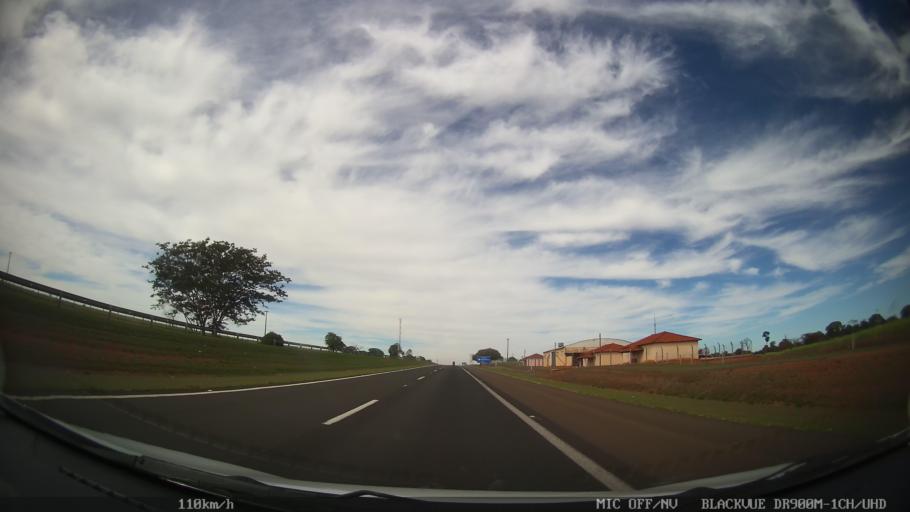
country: BR
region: Sao Paulo
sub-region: Taquaritinga
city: Taquaritinga
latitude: -21.4821
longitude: -48.5893
